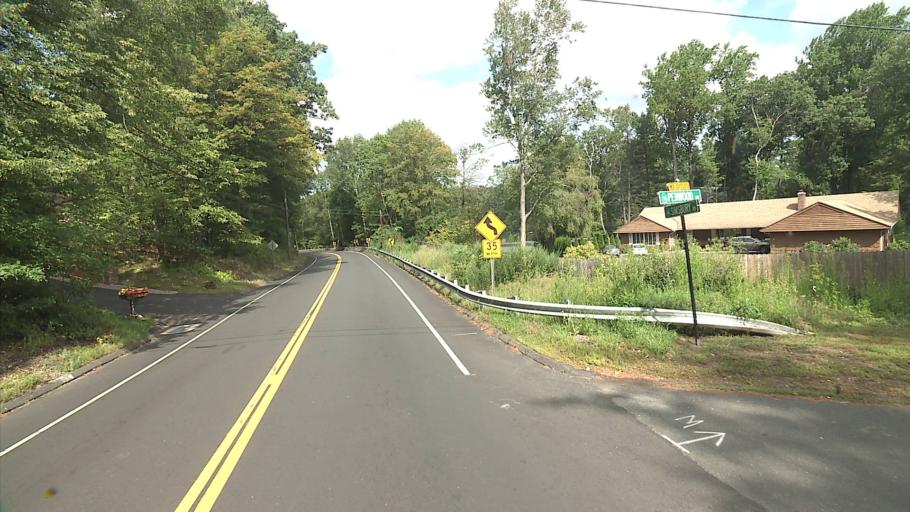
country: US
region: Connecticut
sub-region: Hartford County
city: Weatogue
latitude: 41.8368
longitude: -72.7811
